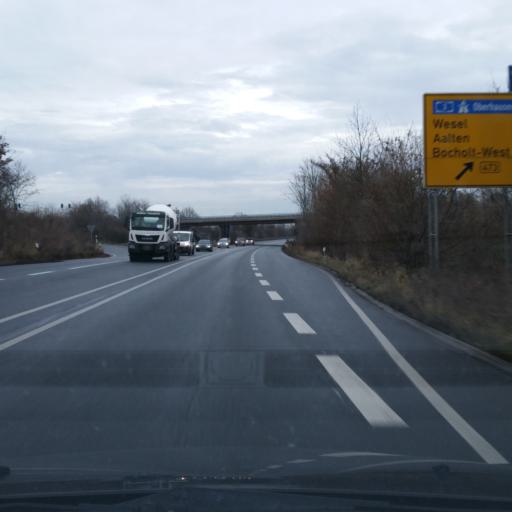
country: DE
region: North Rhine-Westphalia
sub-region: Regierungsbezirk Dusseldorf
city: Bocholt
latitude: 51.8168
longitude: 6.5942
